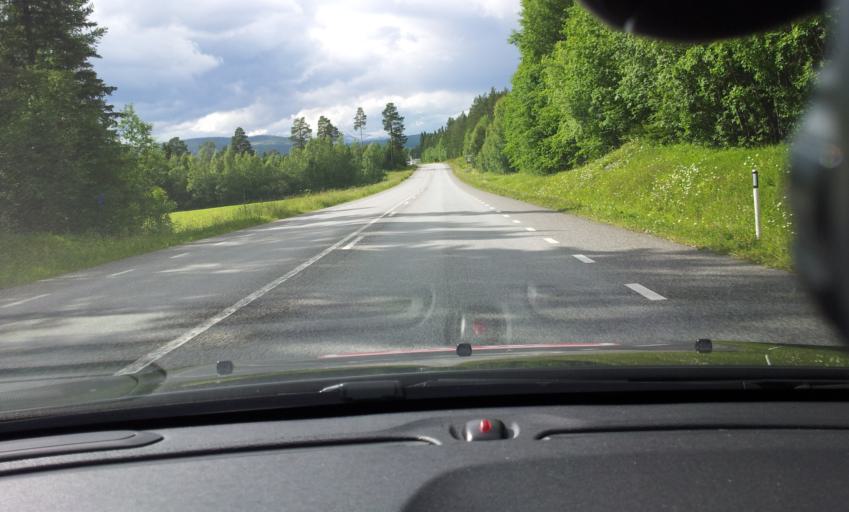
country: SE
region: Jaemtland
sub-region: Are Kommun
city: Jarpen
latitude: 63.3381
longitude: 13.4979
